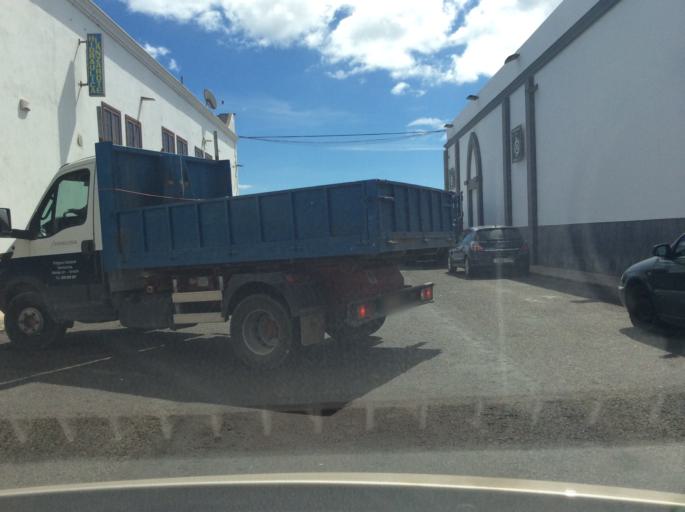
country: ES
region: Canary Islands
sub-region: Provincia de Las Palmas
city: Arrecife
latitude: 28.9728
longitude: -13.5338
